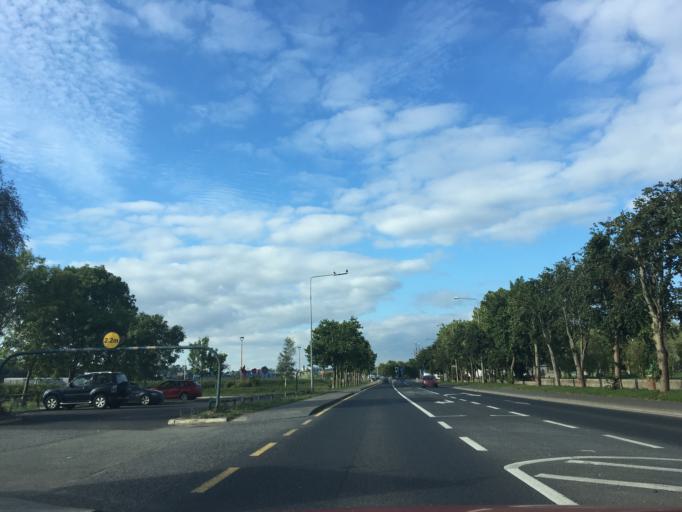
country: IE
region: Leinster
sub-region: Loch Garman
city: New Ross
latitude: 52.3900
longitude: -6.9510
